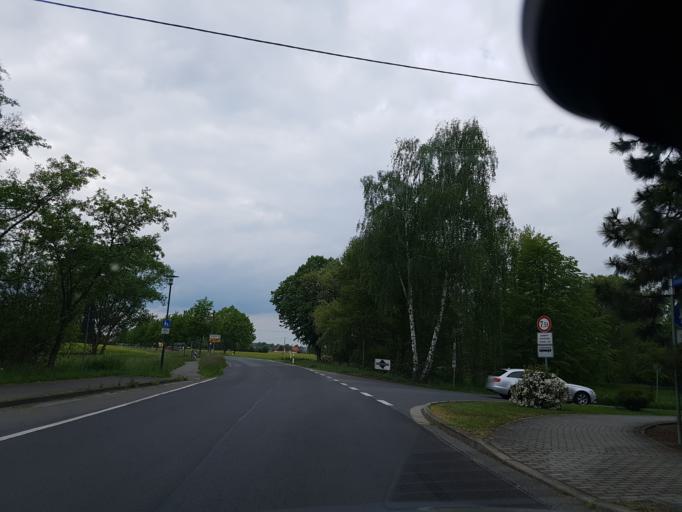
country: DE
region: Brandenburg
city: Luckau
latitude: 51.8541
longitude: 13.7387
